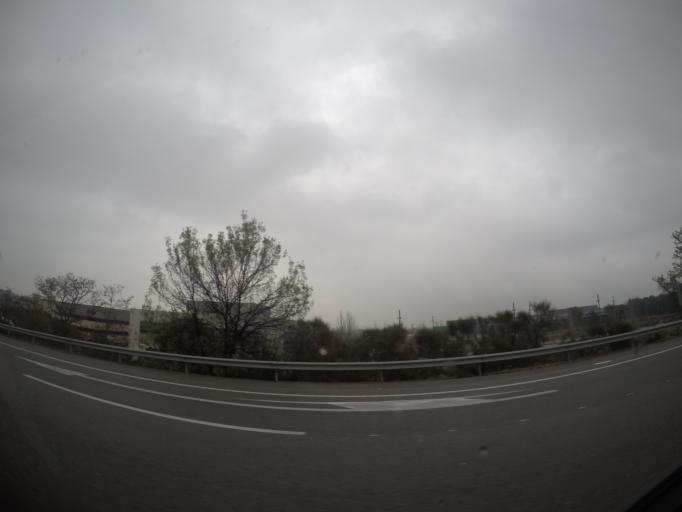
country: ES
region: Catalonia
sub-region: Provincia de Barcelona
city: Vilafranca del Penedes
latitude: 41.3281
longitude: 1.6869
